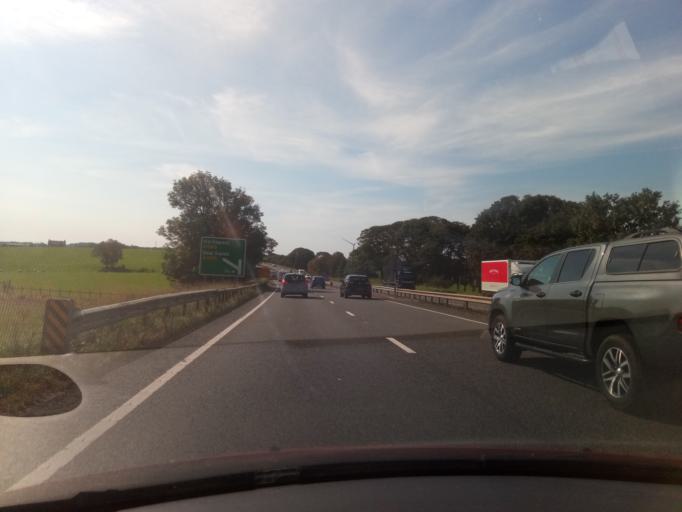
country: GB
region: England
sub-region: Hartlepool
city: Elwick
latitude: 54.6640
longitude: -1.3020
